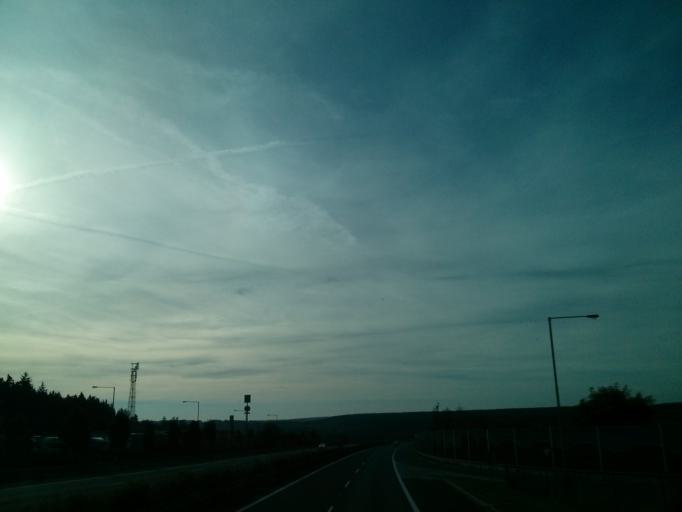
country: CZ
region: Plzensky
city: Dobrany
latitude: 49.6774
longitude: 13.3274
